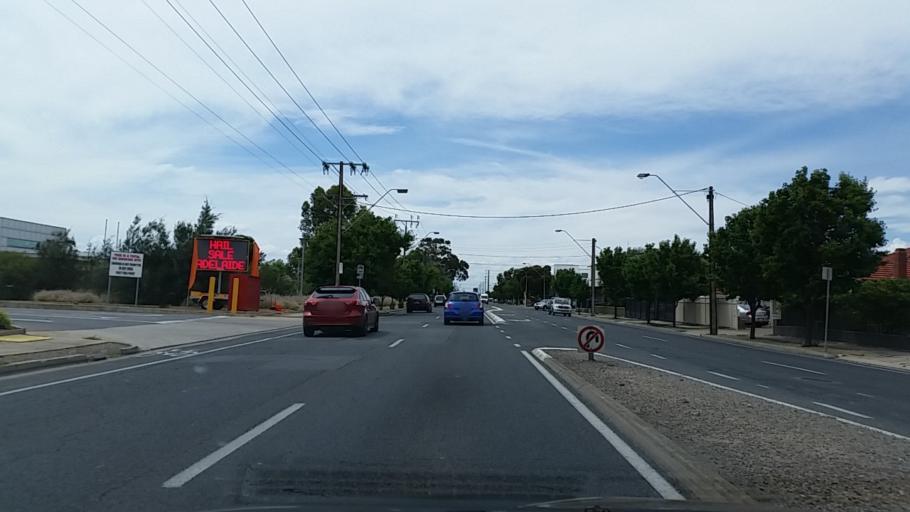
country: AU
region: South Australia
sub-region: City of West Torrens
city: Plympton
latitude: -34.9470
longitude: 138.5535
